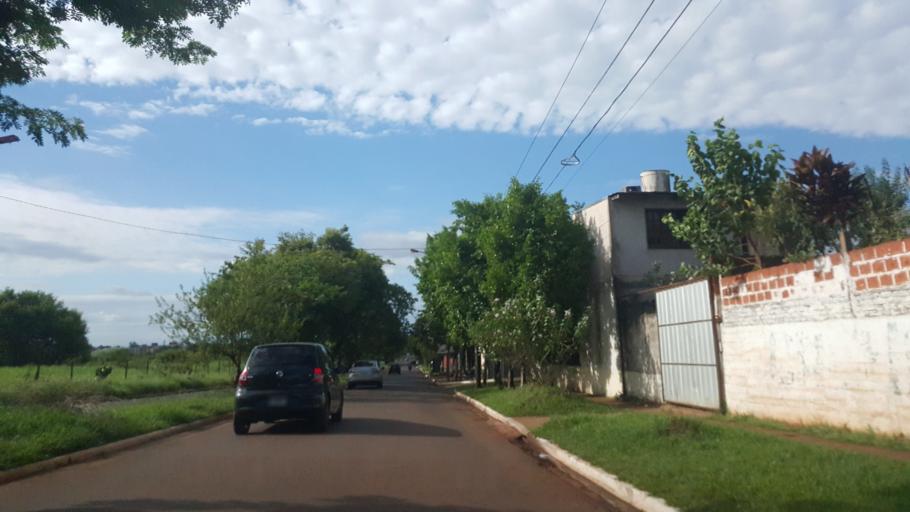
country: AR
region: Misiones
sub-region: Departamento de Capital
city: Posadas
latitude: -27.3771
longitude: -55.9331
